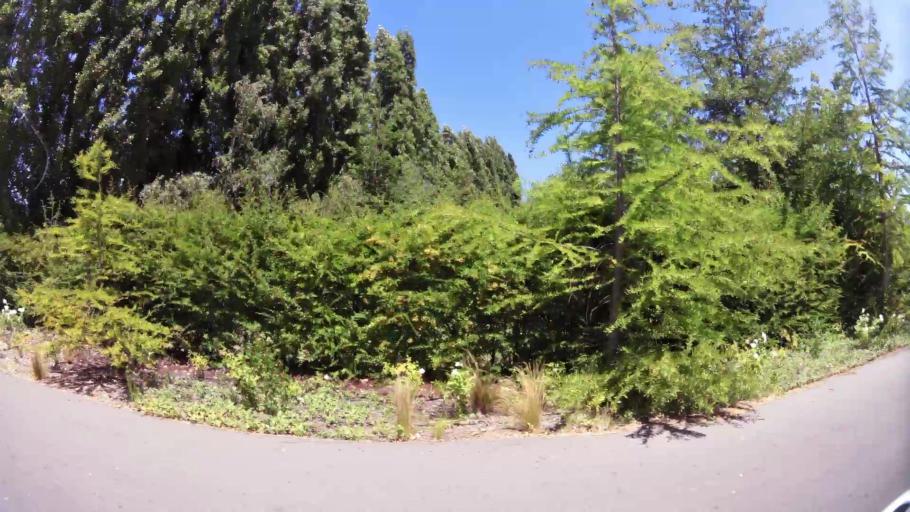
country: CL
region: Maule
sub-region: Provincia de Curico
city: Curico
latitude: -34.9973
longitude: -71.2130
